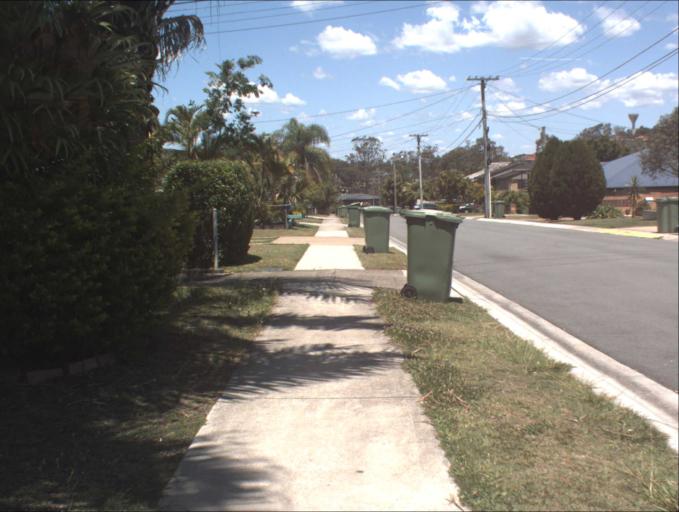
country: AU
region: Queensland
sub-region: Logan
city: Rochedale South
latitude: -27.6029
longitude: 153.1140
